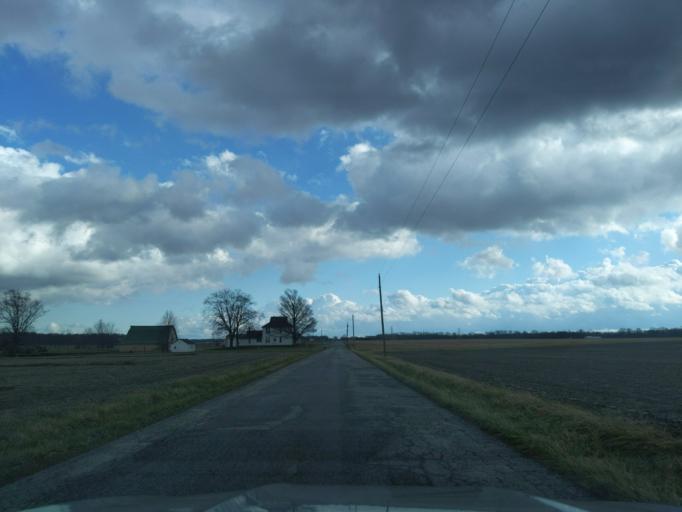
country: US
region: Indiana
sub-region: Decatur County
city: Saint Paul
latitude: 39.4092
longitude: -85.5423
